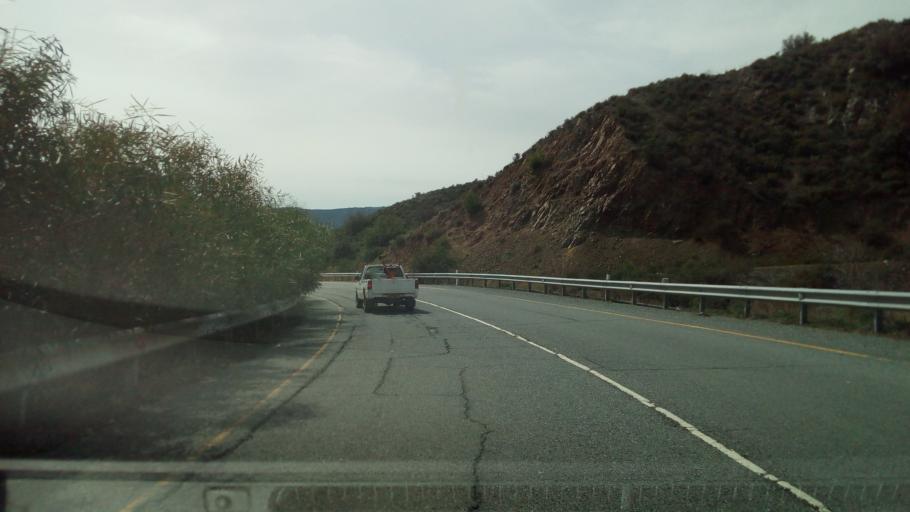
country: CY
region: Limassol
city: Pelendri
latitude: 34.8713
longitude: 32.9297
